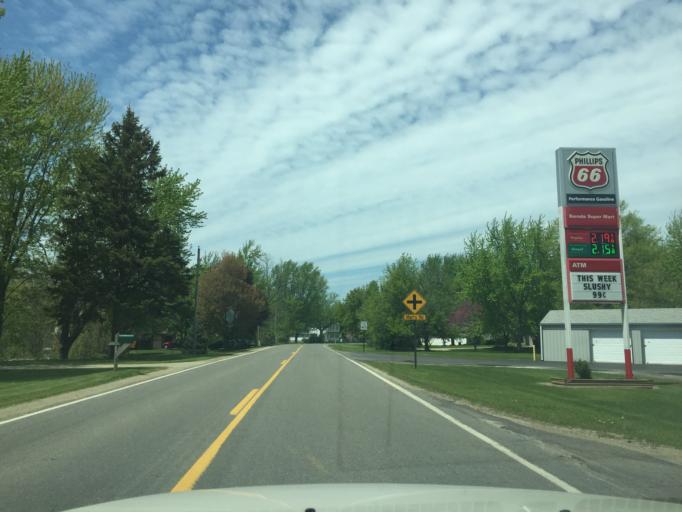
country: US
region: Michigan
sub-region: Berrien County
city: Stevensville
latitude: 41.9776
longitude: -86.4956
